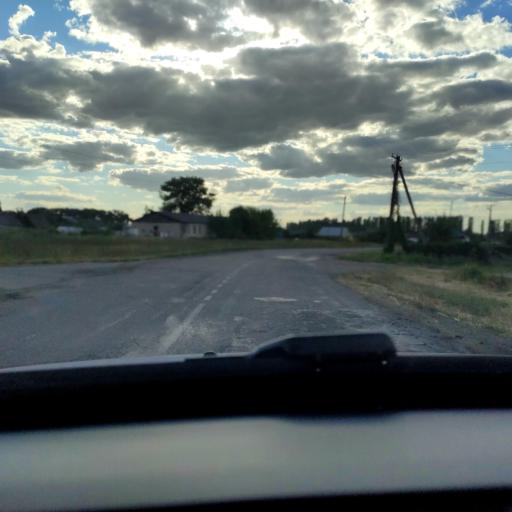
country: RU
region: Voronezj
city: Verkhnyaya Khava
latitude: 51.6130
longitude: 39.8104
